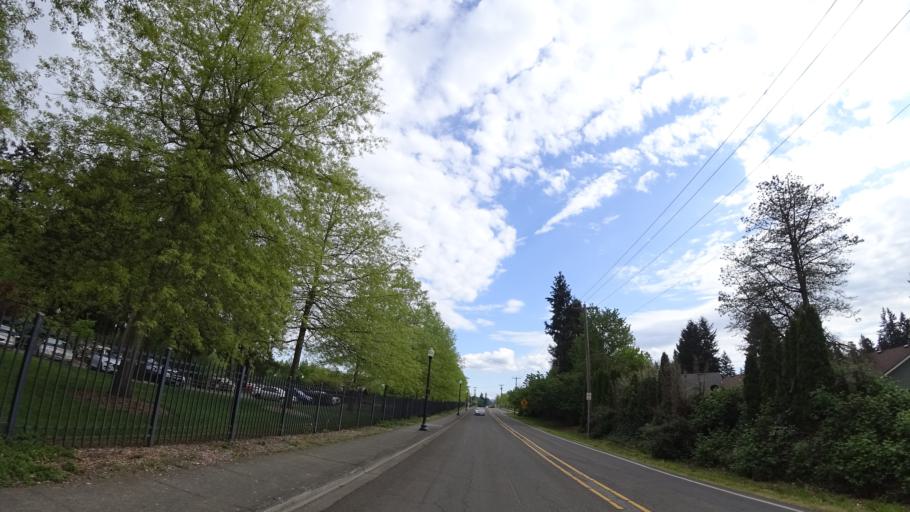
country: US
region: Oregon
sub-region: Washington County
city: Hillsboro
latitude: 45.4933
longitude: -122.9526
